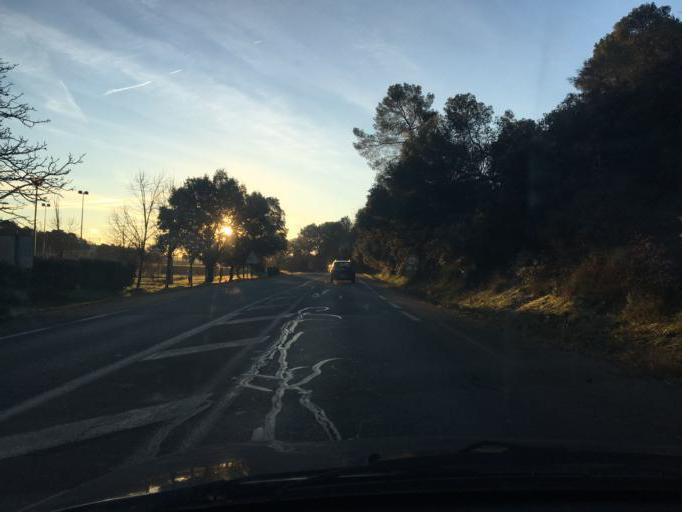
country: FR
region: Provence-Alpes-Cote d'Azur
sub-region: Departement du Var
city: Taradeau
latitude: 43.4515
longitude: 6.4303
